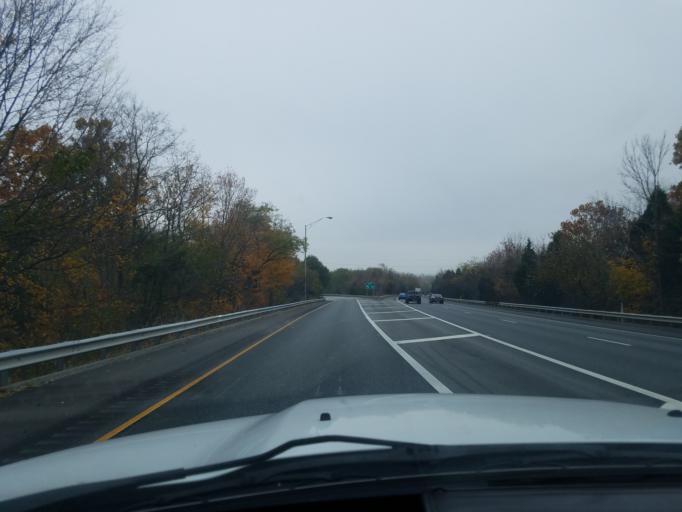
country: US
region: Indiana
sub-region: Floyd County
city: New Albany
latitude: 38.3016
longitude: -85.8547
